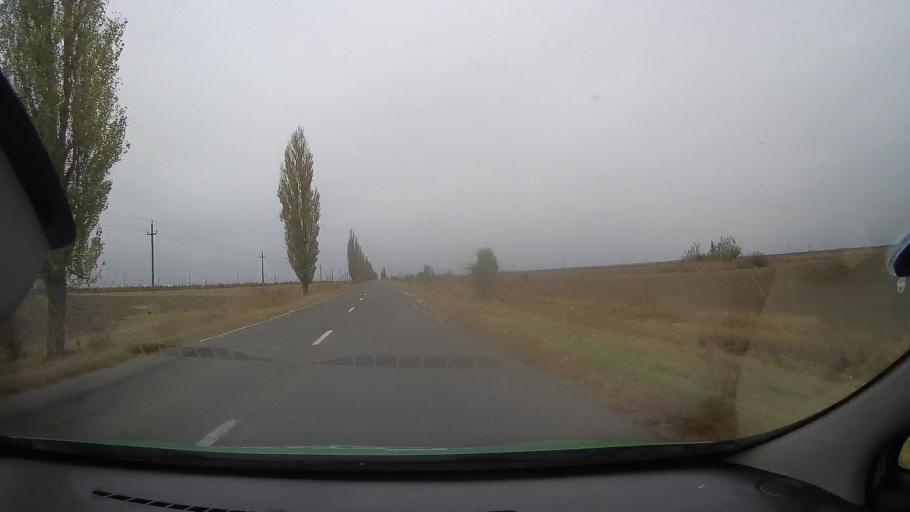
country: RO
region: Ialomita
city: Tandarei
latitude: 44.6568
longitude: 27.6511
